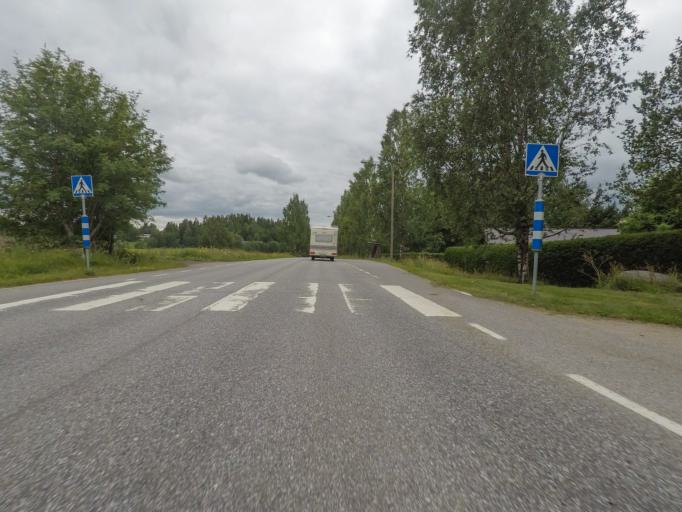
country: FI
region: Varsinais-Suomi
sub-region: Salo
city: Muurla
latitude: 60.3571
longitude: 23.2902
